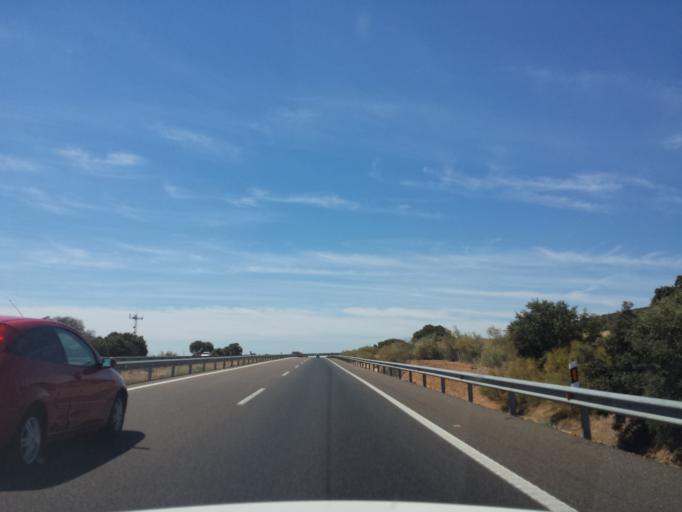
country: ES
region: Extremadura
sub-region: Provincia de Badajoz
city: San Pedro de Merida
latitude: 38.9755
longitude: -6.1467
